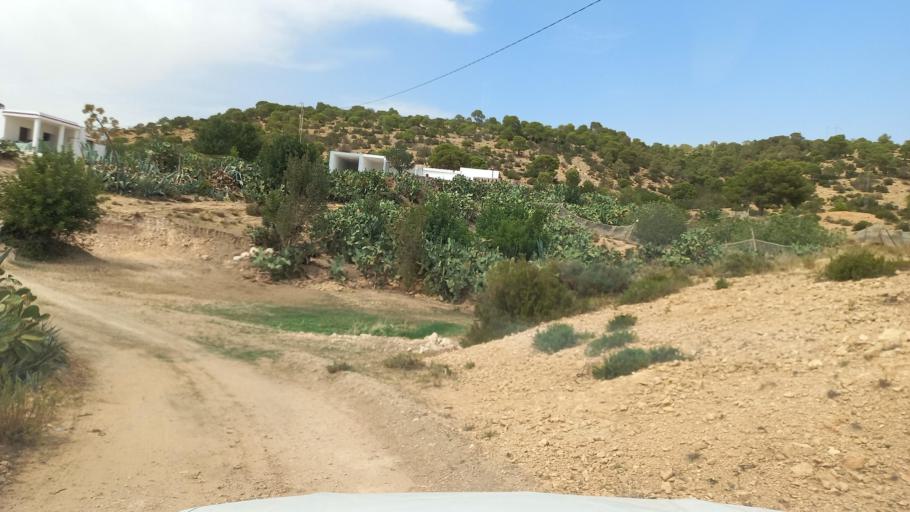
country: TN
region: Al Qasrayn
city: Kasserine
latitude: 35.3735
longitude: 8.8911
